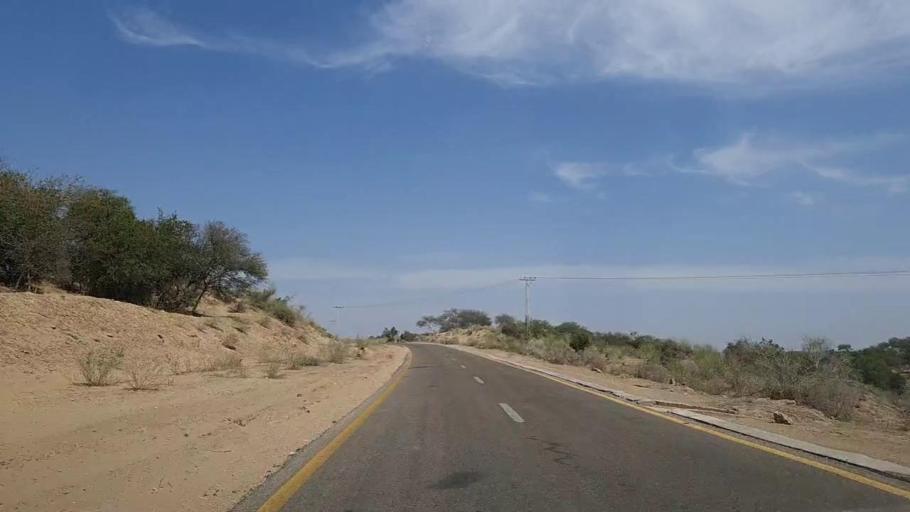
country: PK
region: Sindh
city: Mithi
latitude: 24.8318
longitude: 69.8307
